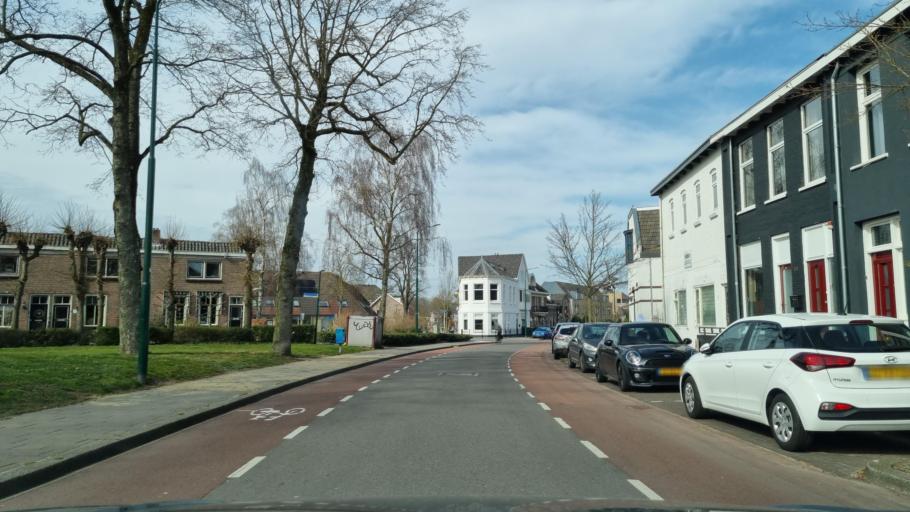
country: NL
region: Utrecht
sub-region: Gemeente Veenendaal
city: Veenendaal
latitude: 52.0315
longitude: 5.5546
